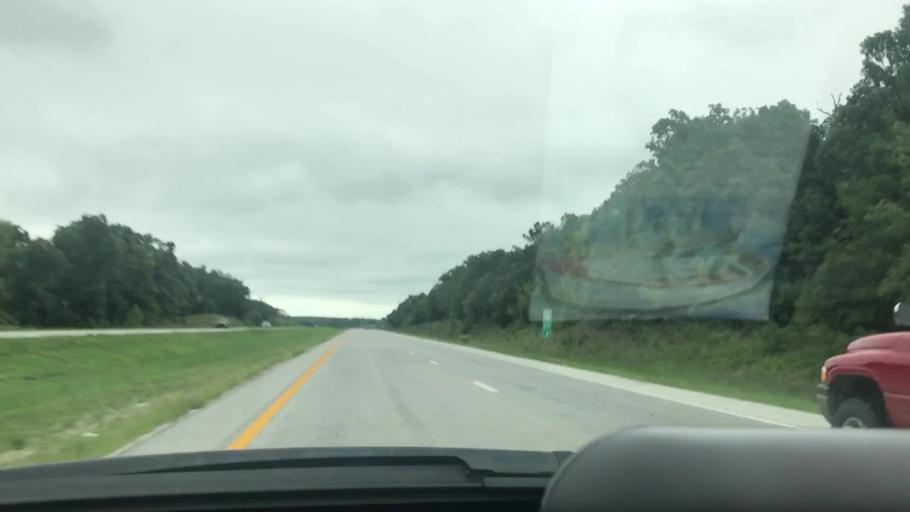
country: US
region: Missouri
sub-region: Greene County
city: Strafford
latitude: 37.2844
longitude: -93.1958
